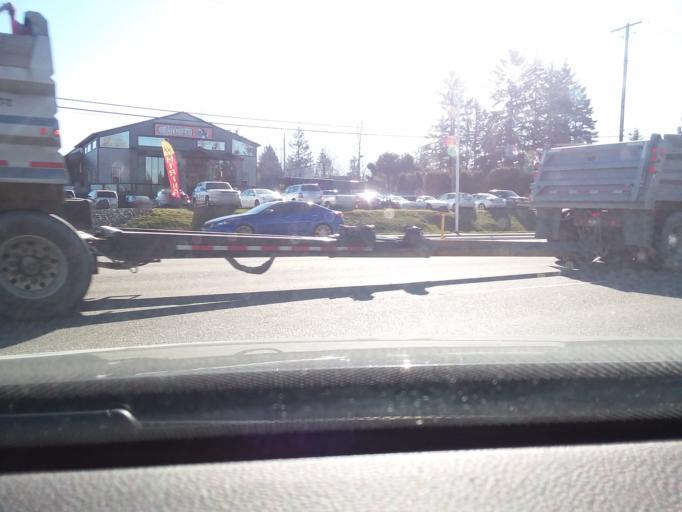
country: US
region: Washington
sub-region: Pierce County
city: Summit
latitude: 47.1366
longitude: -122.3576
